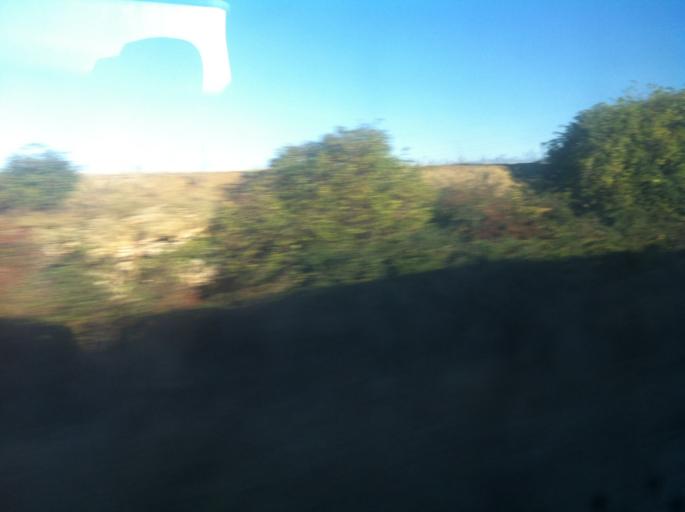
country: ES
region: Castille and Leon
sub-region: Provincia de Palencia
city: Reinoso de Cerrato
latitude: 42.0052
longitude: -4.3508
